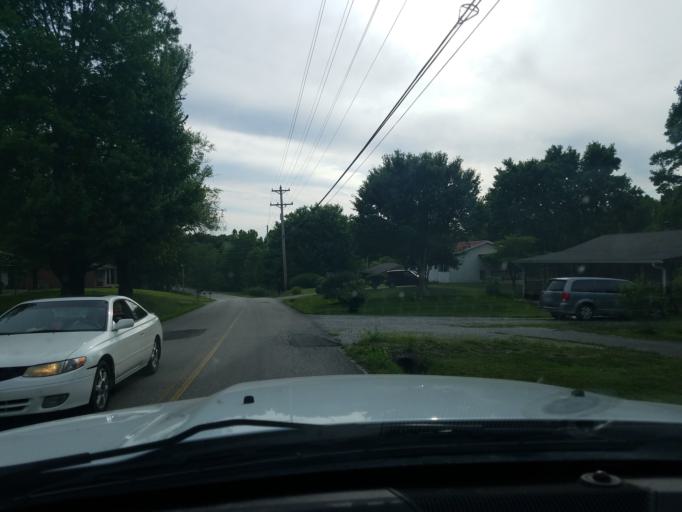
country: US
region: Tennessee
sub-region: Putnam County
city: Baxter
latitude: 36.1289
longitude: -85.6040
